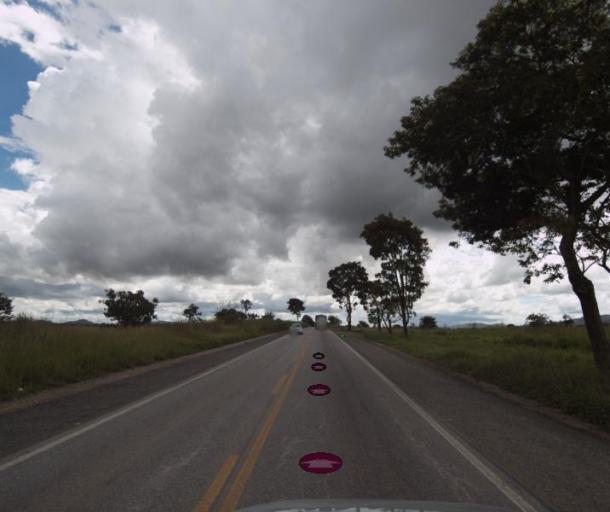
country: BR
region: Goias
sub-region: Uruacu
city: Uruacu
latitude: -14.2615
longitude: -49.1427
